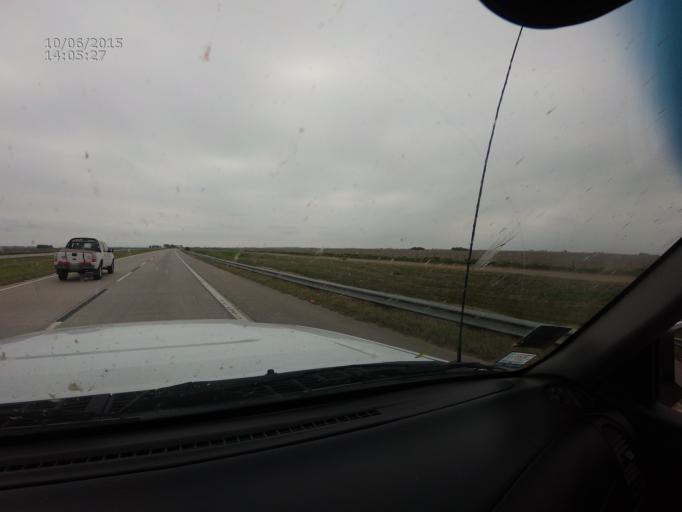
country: AR
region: Cordoba
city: Morrison
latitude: -32.5112
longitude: -62.9941
